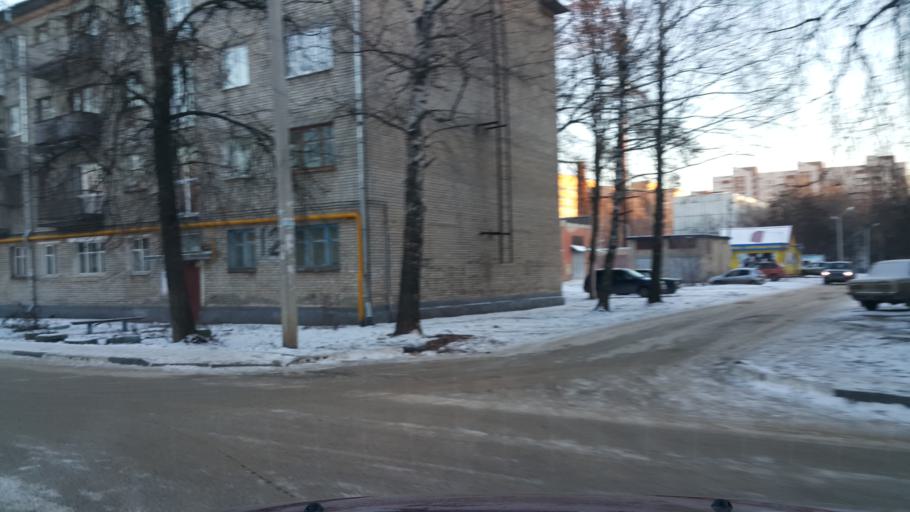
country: RU
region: Tambov
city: Pokrovo-Prigorodnoye
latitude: 52.7076
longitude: 41.3943
